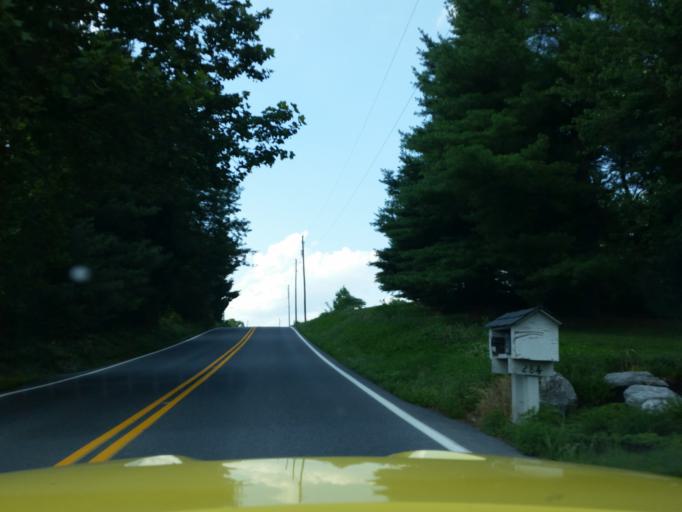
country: US
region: Pennsylvania
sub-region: Lancaster County
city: Salunga
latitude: 40.1372
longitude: -76.4525
